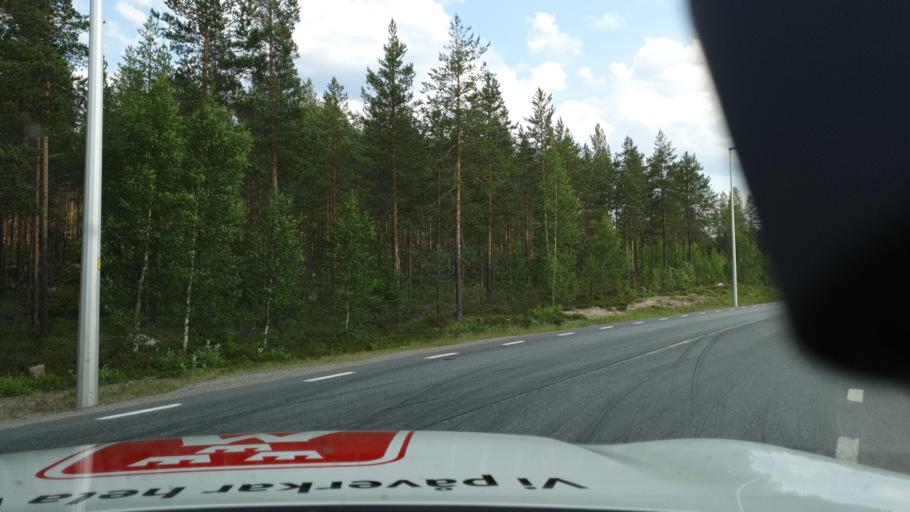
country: SE
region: Vaesterbotten
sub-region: Skelleftea Kommun
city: Ursviken
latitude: 64.6520
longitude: 21.1471
